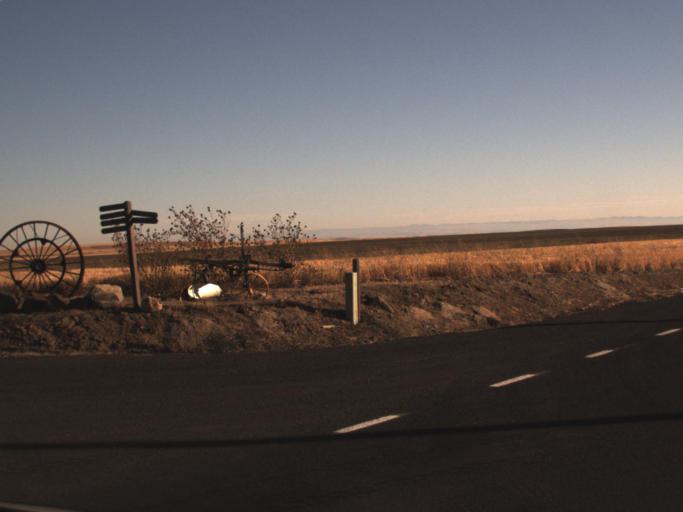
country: US
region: Washington
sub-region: Adams County
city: Ritzville
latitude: 46.8684
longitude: -118.3358
